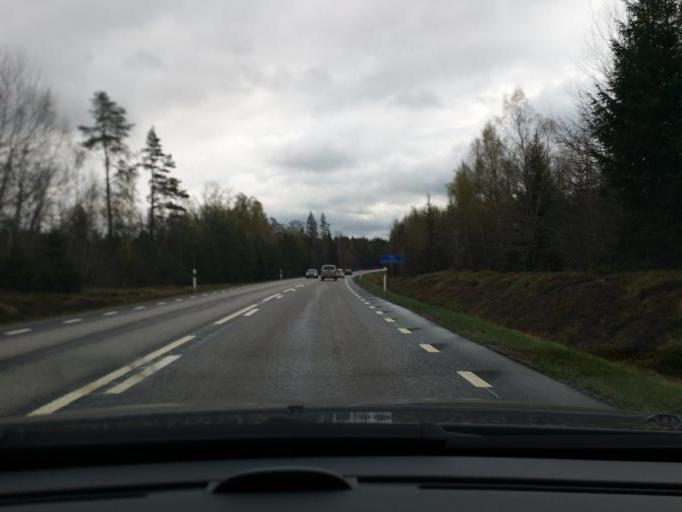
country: SE
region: Kronoberg
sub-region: Vaxjo Kommun
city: Ingelstad
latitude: 56.8070
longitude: 14.8881
